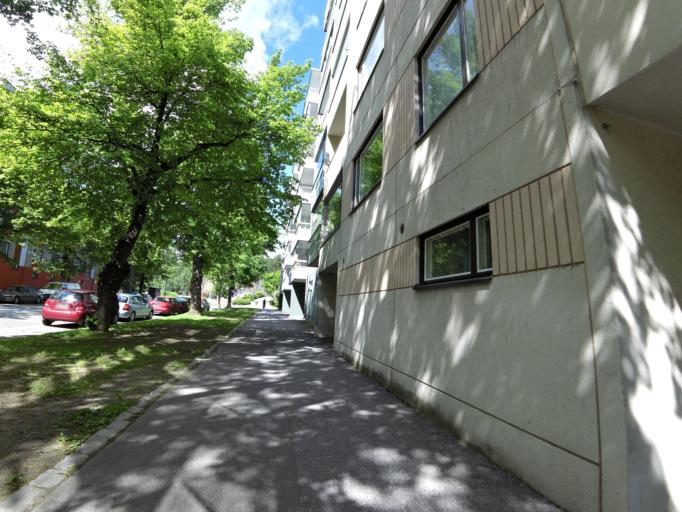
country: FI
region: Pirkanmaa
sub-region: Tampere
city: Tampere
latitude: 61.5059
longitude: 23.7796
